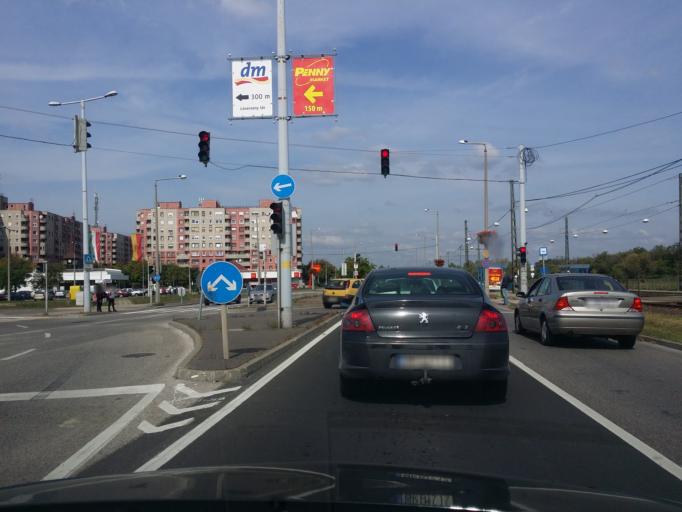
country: HU
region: Budapest
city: Budapest XV. keruelet
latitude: 47.5774
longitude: 19.1157
